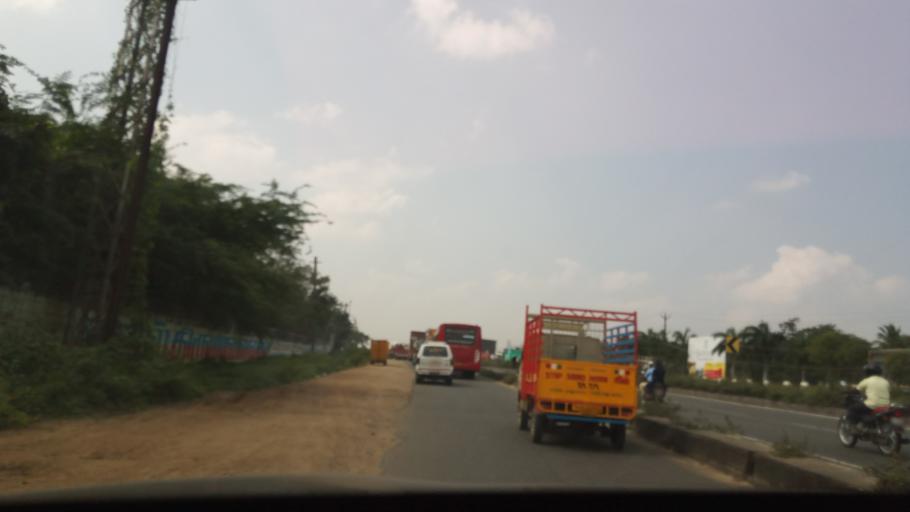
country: IN
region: Tamil Nadu
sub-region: Kancheepuram
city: Sriperumbudur
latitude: 12.9537
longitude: 79.9348
